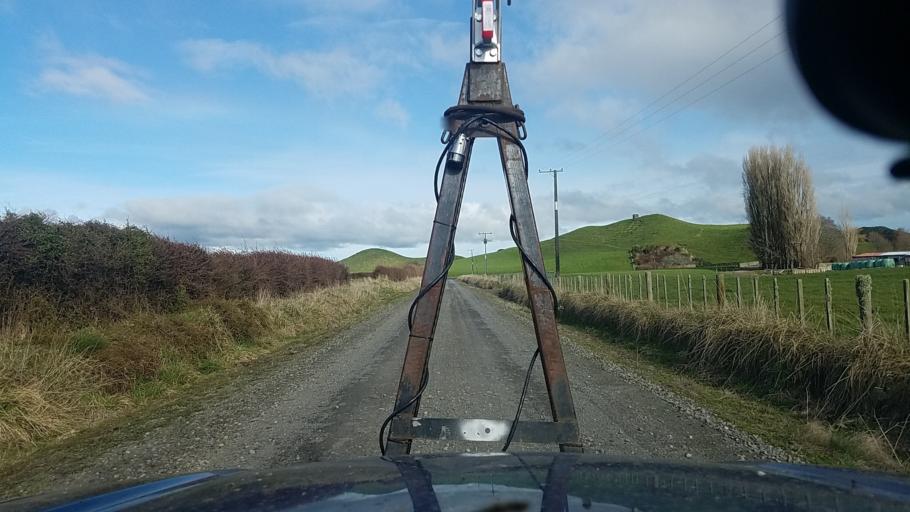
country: NZ
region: Taranaki
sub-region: South Taranaki District
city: Eltham
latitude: -39.3456
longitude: 174.4207
